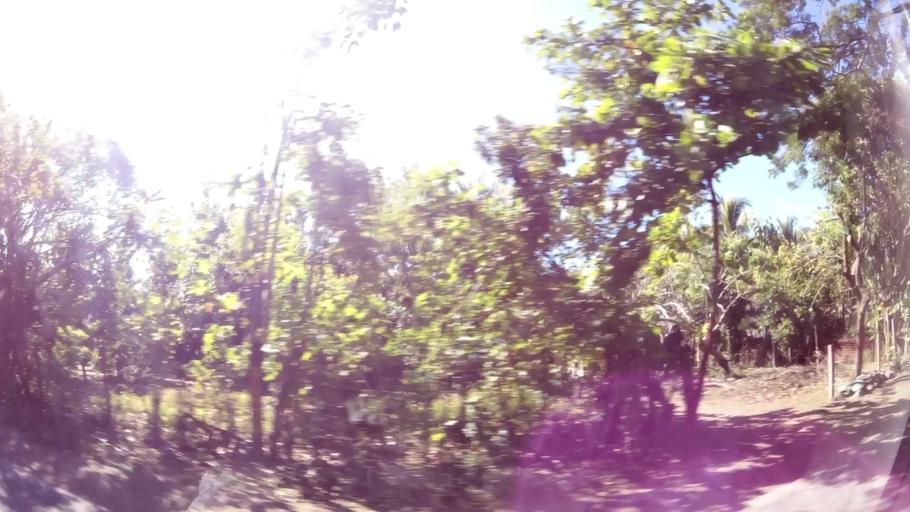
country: GT
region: Escuintla
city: Iztapa
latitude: 13.9225
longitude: -90.5731
